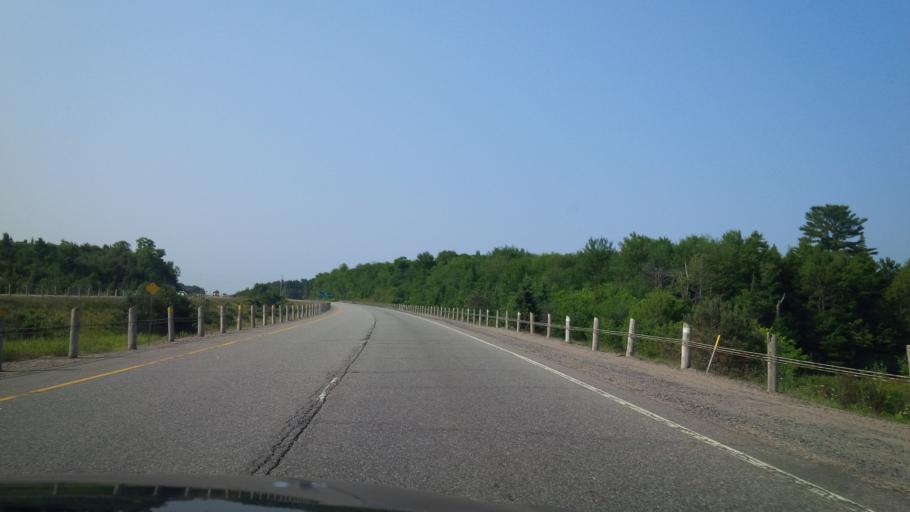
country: CA
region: Ontario
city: Huntsville
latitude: 45.2225
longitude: -79.3128
